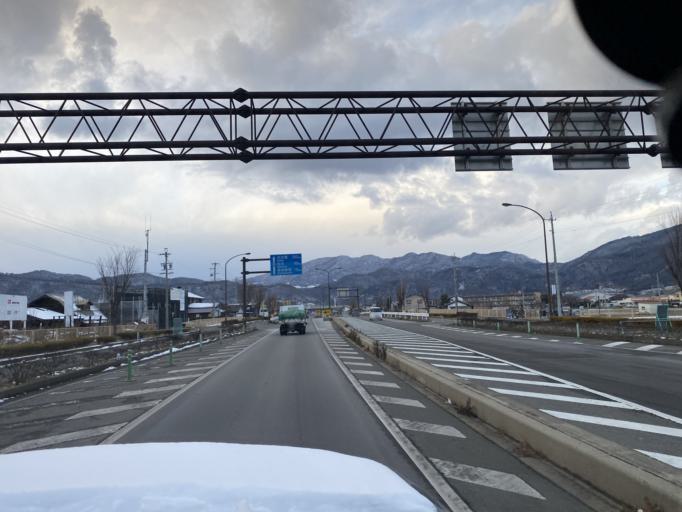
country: JP
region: Nagano
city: Nagano-shi
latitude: 36.6060
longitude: 138.1548
